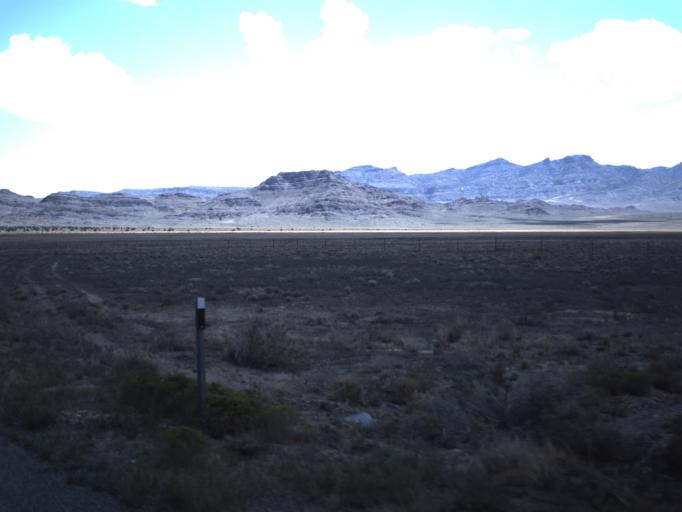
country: US
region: Utah
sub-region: Beaver County
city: Milford
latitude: 39.0610
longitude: -113.7545
